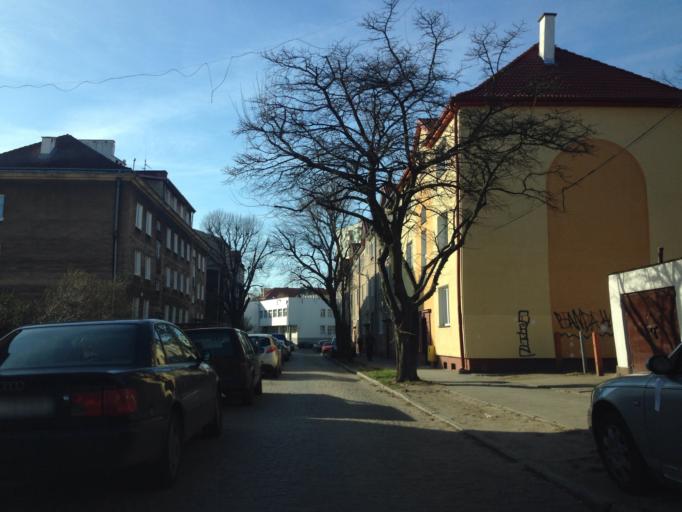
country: PL
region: Pomeranian Voivodeship
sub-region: Gdansk
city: Gdansk
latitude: 54.3851
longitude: 18.6266
